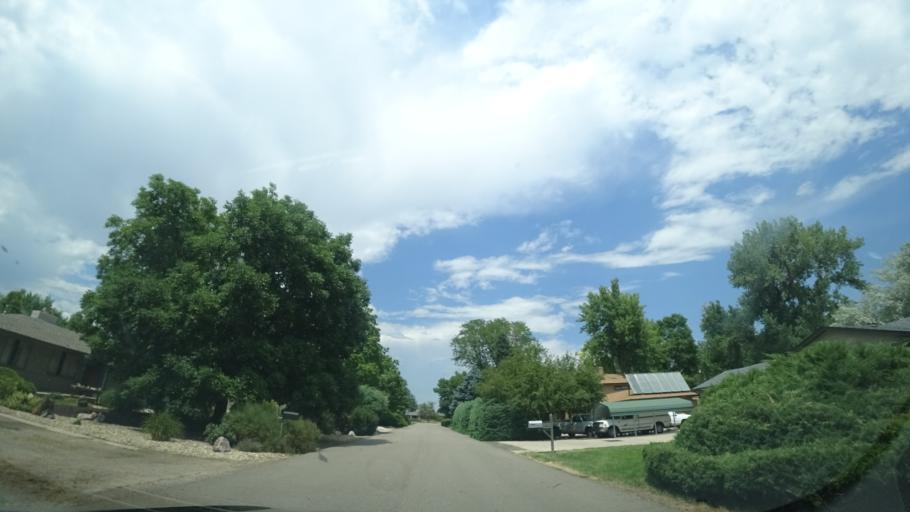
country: US
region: Colorado
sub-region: Jefferson County
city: Lakewood
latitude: 39.7208
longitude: -105.0845
